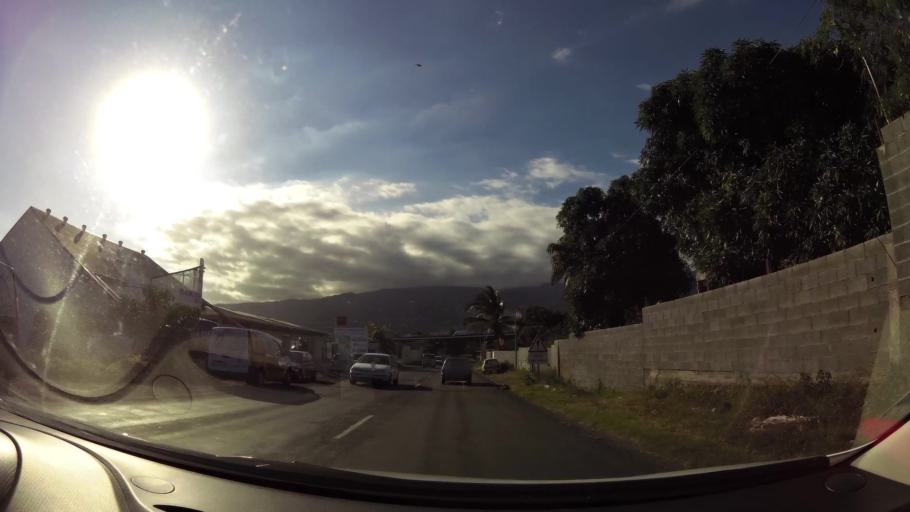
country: RE
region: Reunion
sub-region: Reunion
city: Saint-Louis
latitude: -21.2868
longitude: 55.3977
